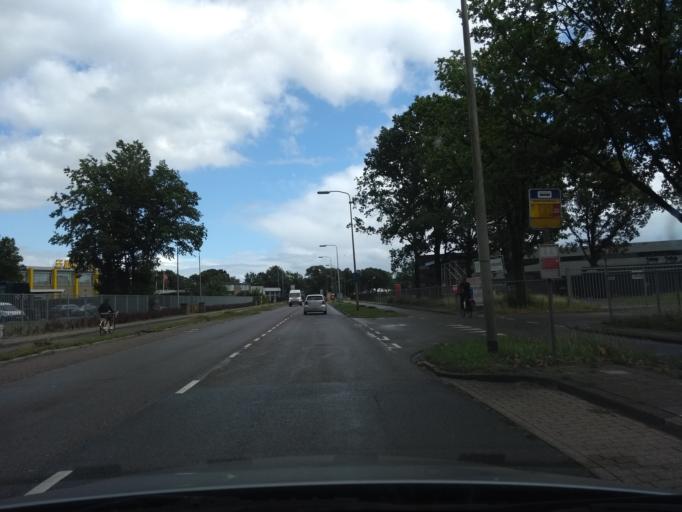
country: NL
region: Overijssel
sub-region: Gemeente Almelo
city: Almelo
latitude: 52.3686
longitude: 6.6465
